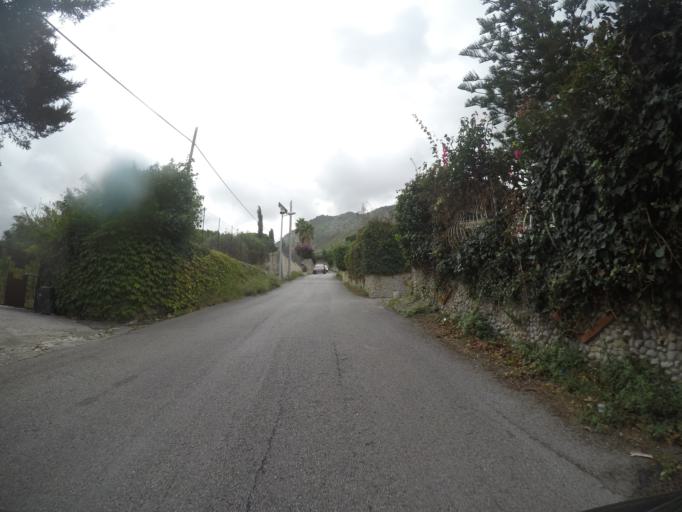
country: IT
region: Sicily
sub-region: Palermo
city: Carini
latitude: 38.1240
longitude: 13.1834
